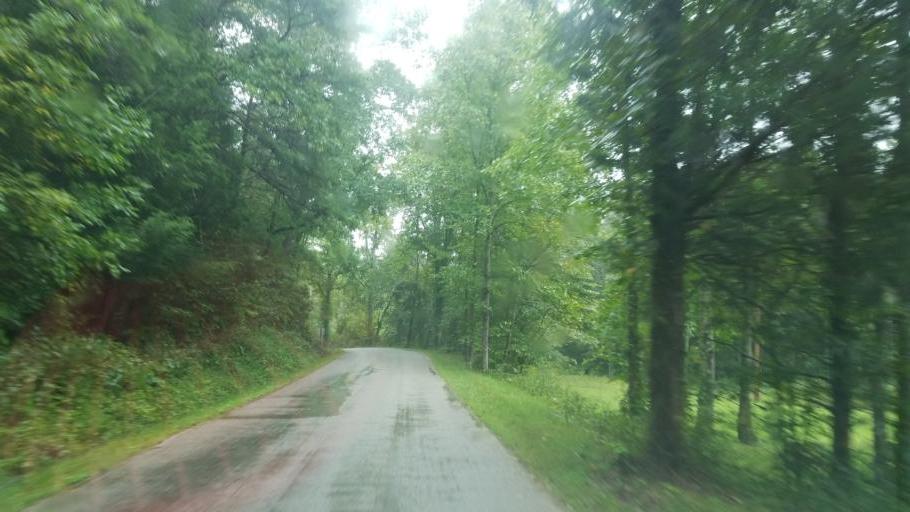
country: US
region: Kentucky
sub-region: Lewis County
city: Vanceburg
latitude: 38.7818
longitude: -83.2588
